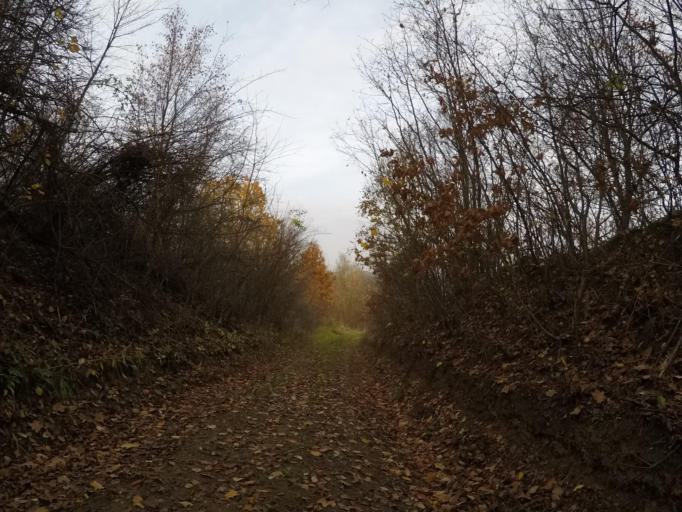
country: SK
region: Presovsky
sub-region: Okres Presov
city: Presov
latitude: 48.9377
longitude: 21.1719
